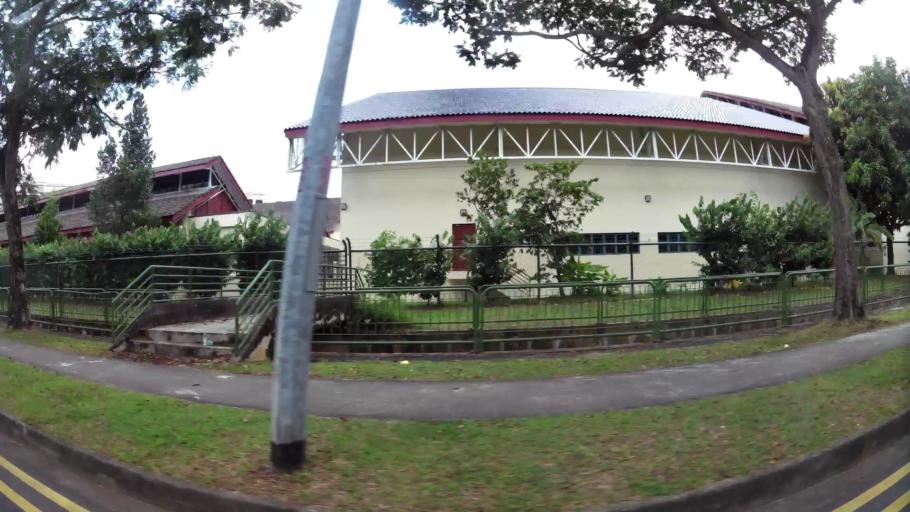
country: MY
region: Johor
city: Kampung Pasir Gudang Baru
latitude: 1.4242
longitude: 103.8296
